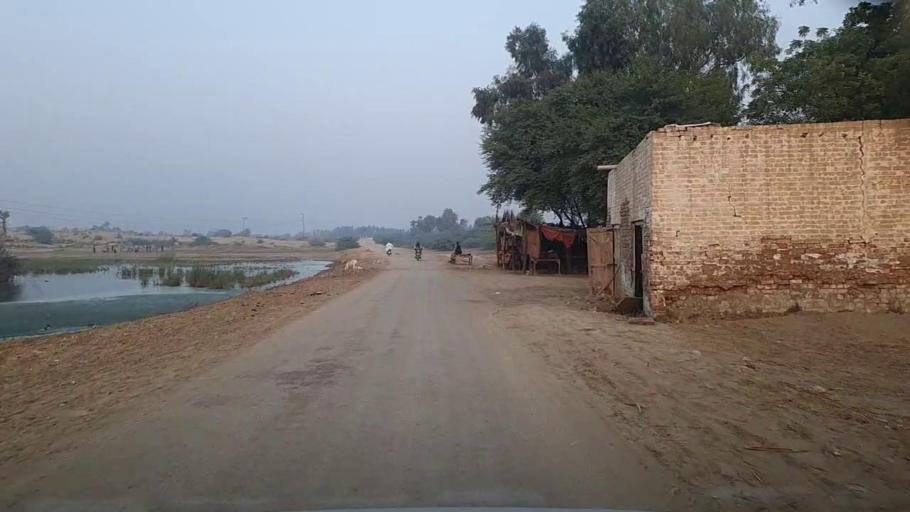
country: PK
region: Sindh
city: Kandiari
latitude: 27.0434
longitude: 68.5904
